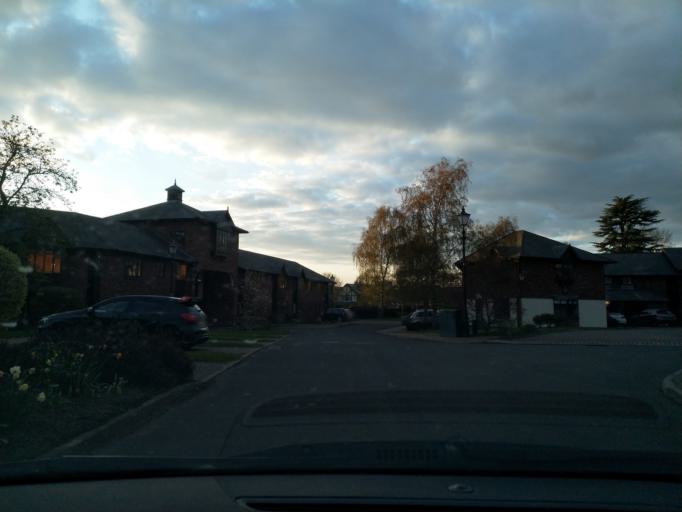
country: GB
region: England
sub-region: Warwickshire
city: Royal Leamington Spa
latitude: 52.2979
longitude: -1.5377
